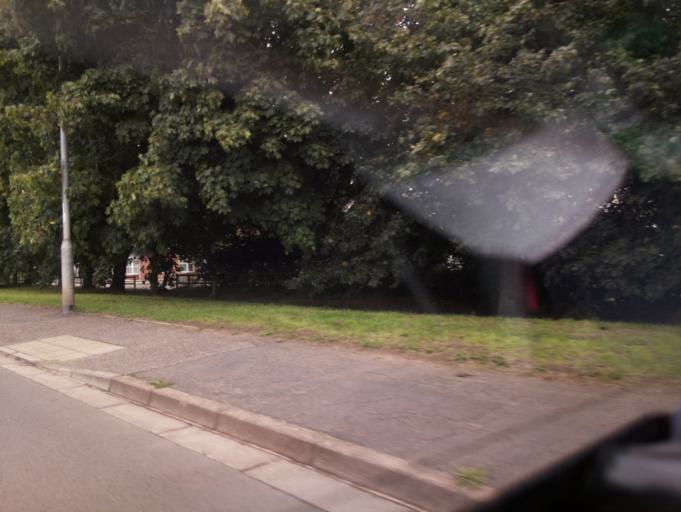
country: GB
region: England
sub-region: Devon
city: Cullompton
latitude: 50.8662
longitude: -3.3916
